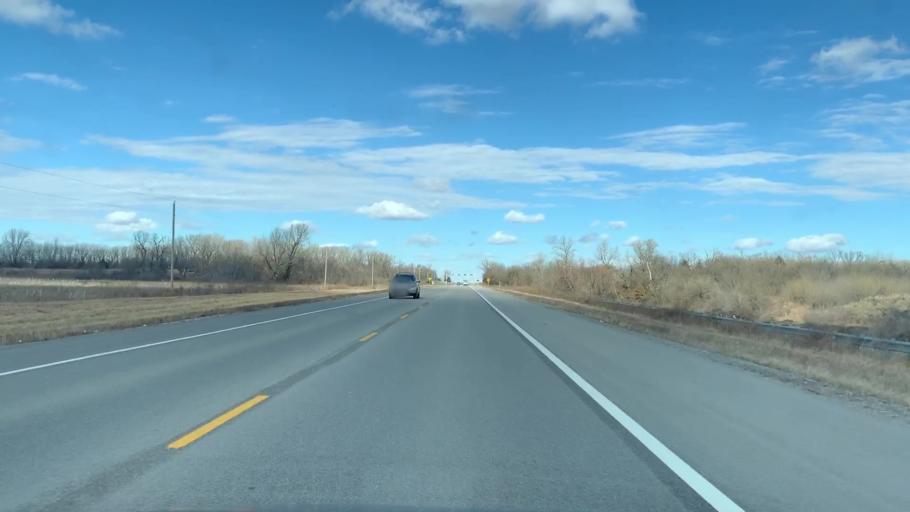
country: US
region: Kansas
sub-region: Cherokee County
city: Columbus
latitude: 37.3170
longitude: -94.8323
